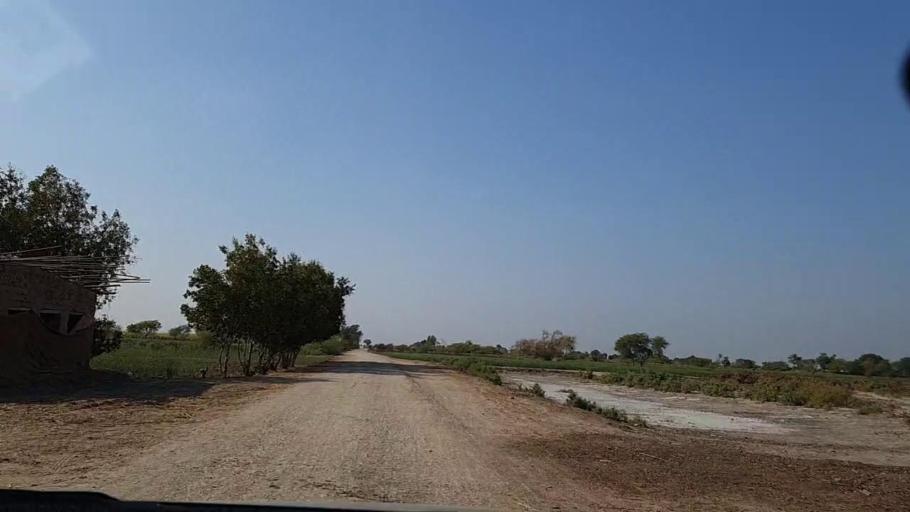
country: PK
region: Sindh
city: Digri
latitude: 25.1794
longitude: 69.0097
